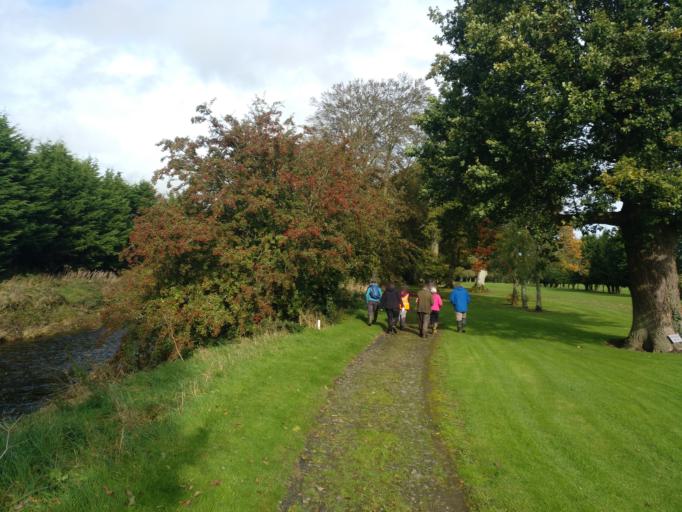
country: IE
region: Leinster
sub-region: Kilkenny
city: Castlecomer
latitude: 52.8011
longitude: -7.2095
